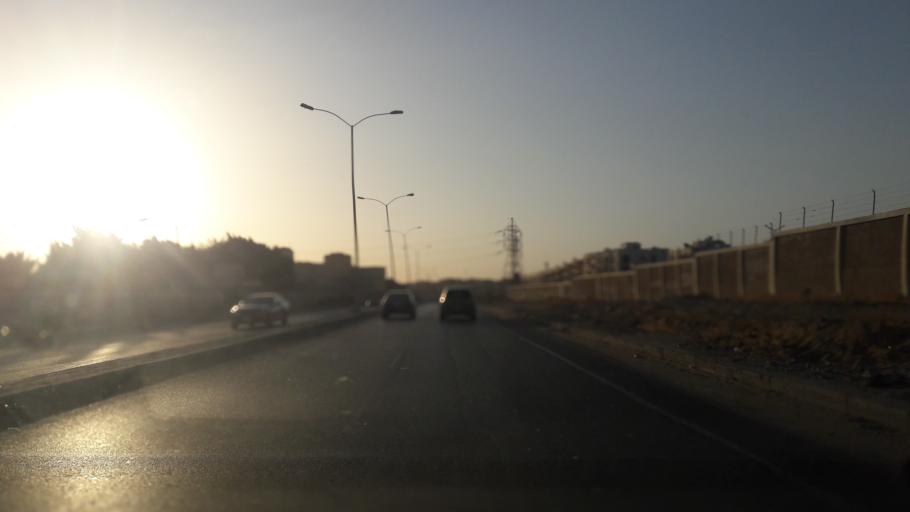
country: EG
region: Al Jizah
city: Madinat Sittah Uktubar
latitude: 29.9469
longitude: 30.9449
